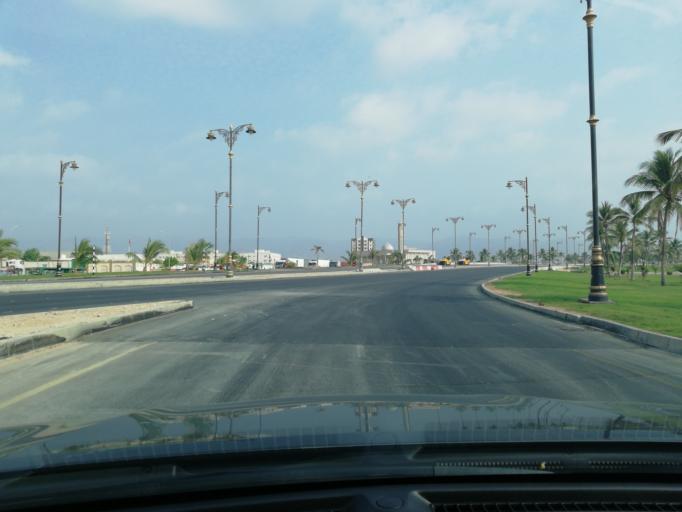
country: OM
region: Zufar
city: Salalah
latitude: 17.0200
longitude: 54.0578
